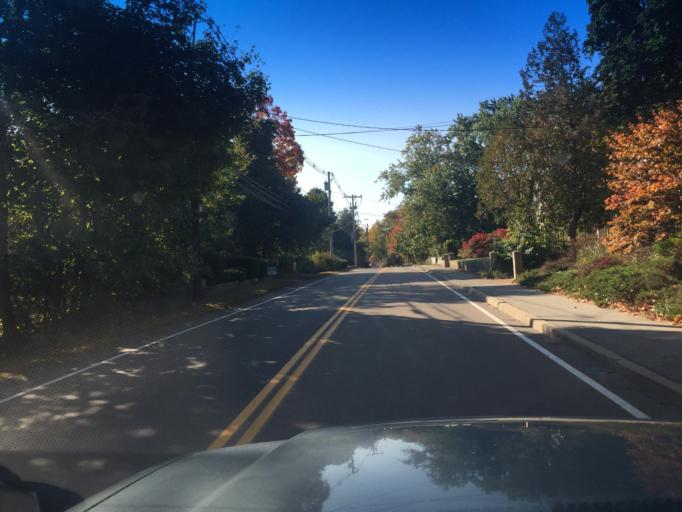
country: US
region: Massachusetts
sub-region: Norfolk County
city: Medway
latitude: 42.1498
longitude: -71.4254
